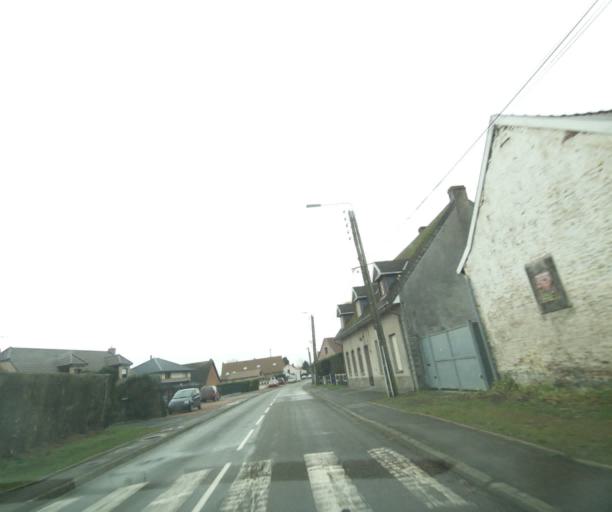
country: FR
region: Nord-Pas-de-Calais
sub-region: Departement du Nord
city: Crespin
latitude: 50.4468
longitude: 3.6558
